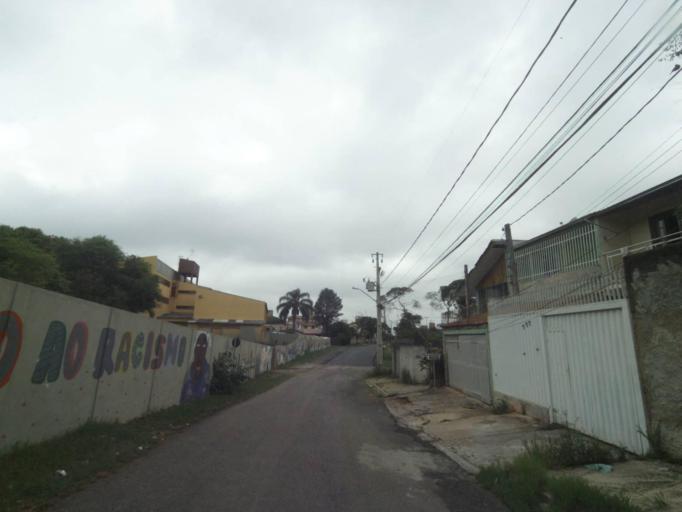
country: BR
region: Parana
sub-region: Curitiba
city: Curitiba
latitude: -25.4876
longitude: -49.3539
